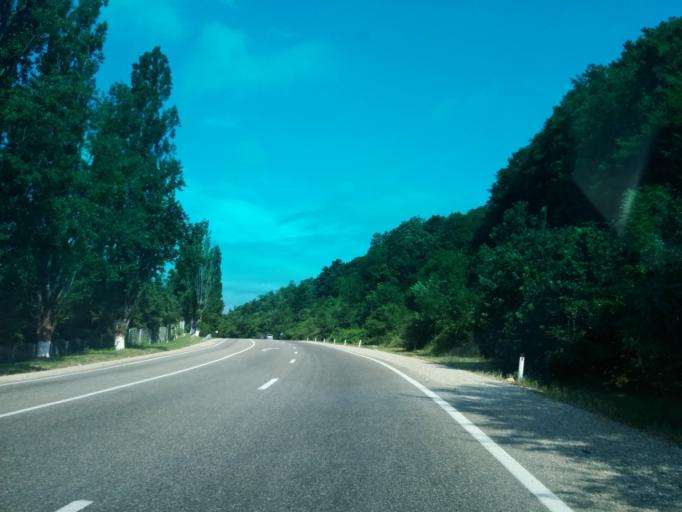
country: RU
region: Krasnodarskiy
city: Nebug
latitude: 44.1521
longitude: 39.0140
